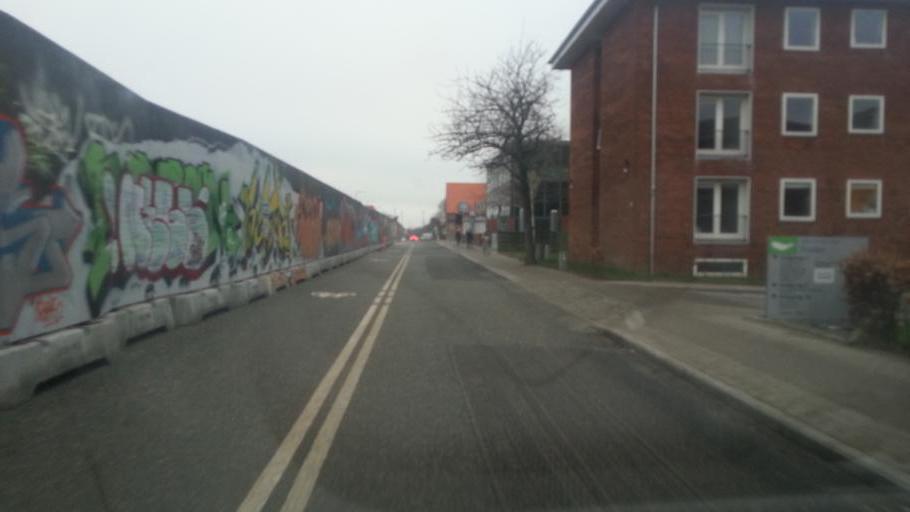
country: DK
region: South Denmark
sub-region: Esbjerg Kommune
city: Esbjerg
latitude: 55.4747
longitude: 8.4590
